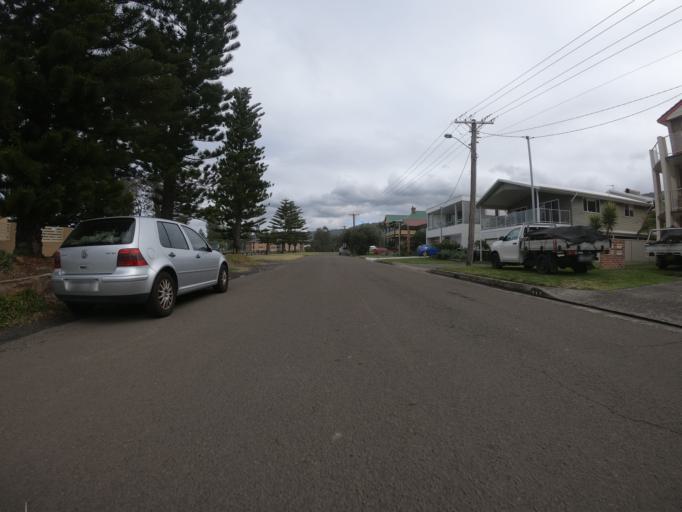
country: AU
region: New South Wales
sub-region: Wollongong
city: Bulli
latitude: -34.3134
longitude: 150.9291
